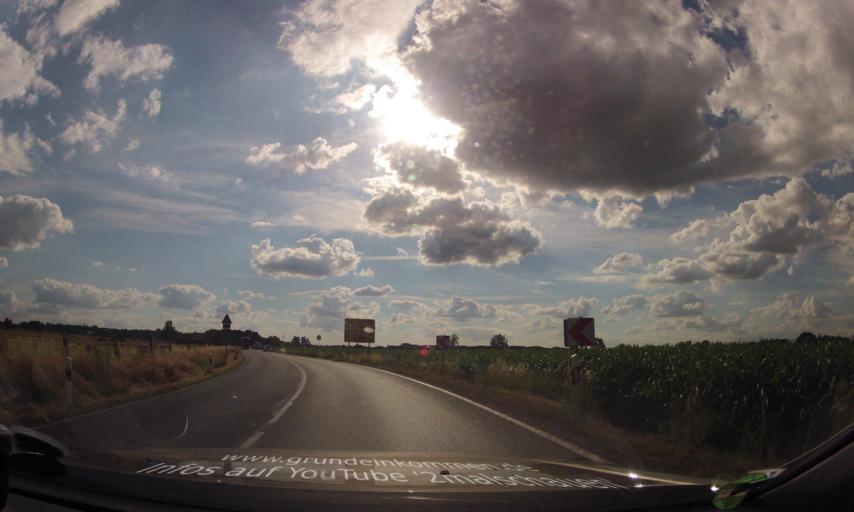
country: DE
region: Saxony
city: Bennewitz
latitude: 51.3614
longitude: 12.6807
